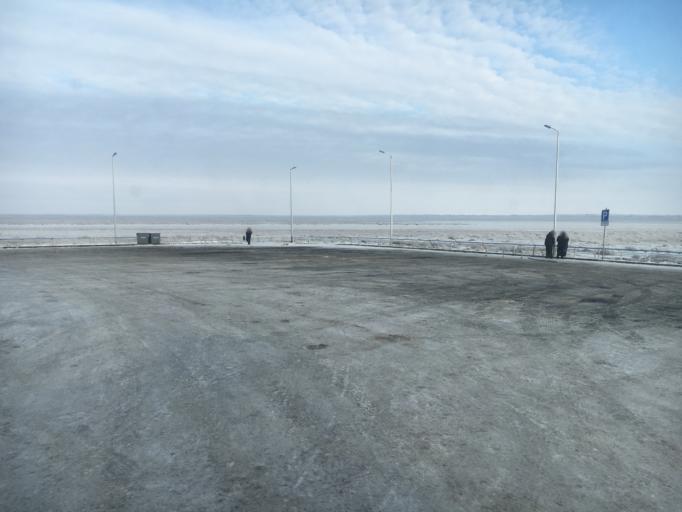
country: KZ
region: Aqtoebe
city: Yrghyz
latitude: 48.5156
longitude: 61.0014
